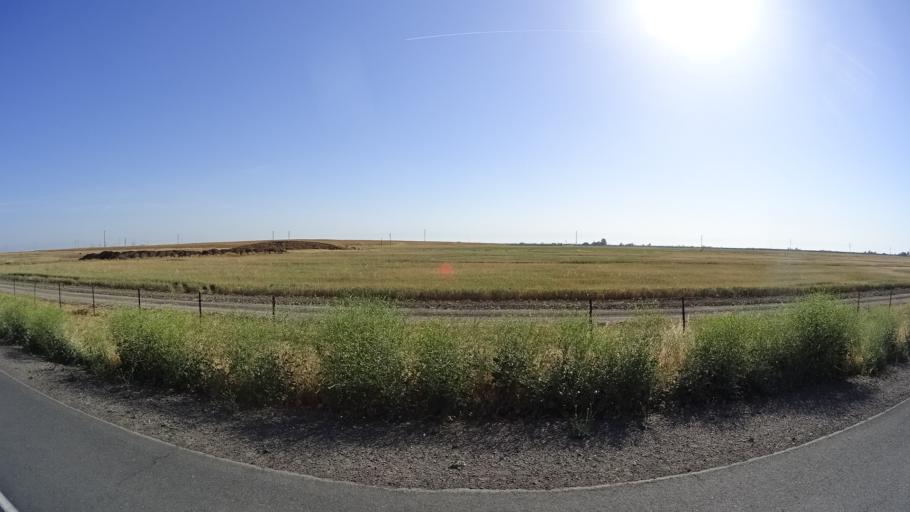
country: US
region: California
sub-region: Kings County
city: Corcoran
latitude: 36.1287
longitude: -119.5785
